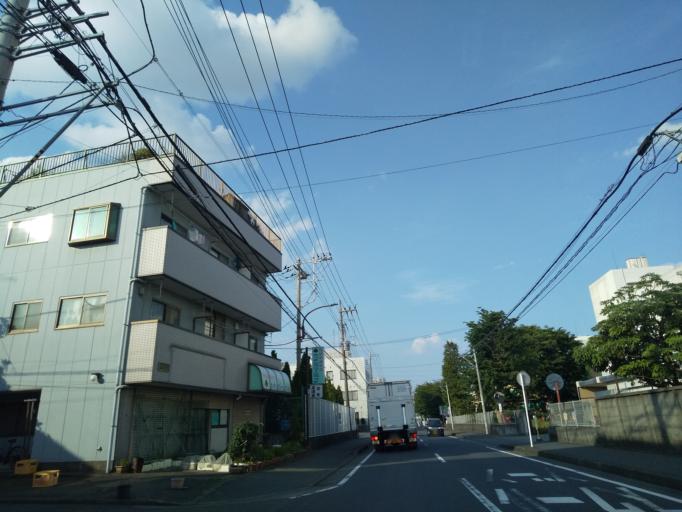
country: JP
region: Tokyo
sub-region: Machida-shi
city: Machida
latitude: 35.5544
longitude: 139.4058
